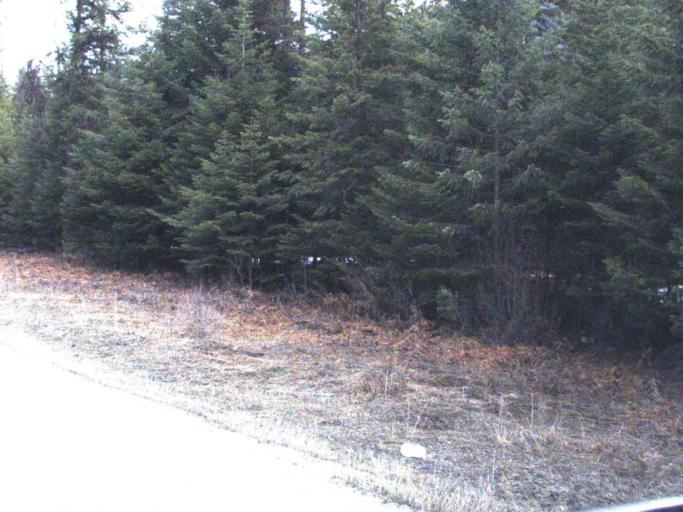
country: US
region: Washington
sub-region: Stevens County
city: Chewelah
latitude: 48.5848
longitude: -117.3519
